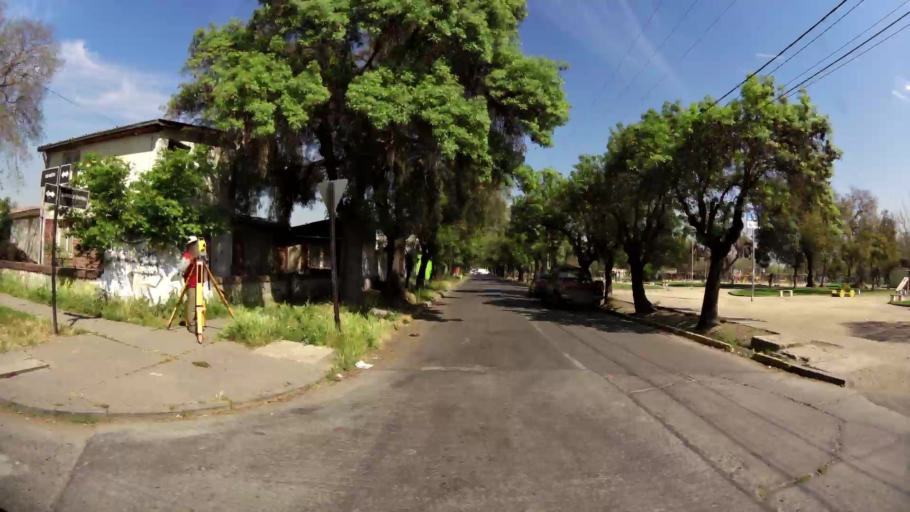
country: CL
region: Santiago Metropolitan
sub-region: Provincia de Maipo
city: San Bernardo
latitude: -33.5906
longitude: -70.6944
